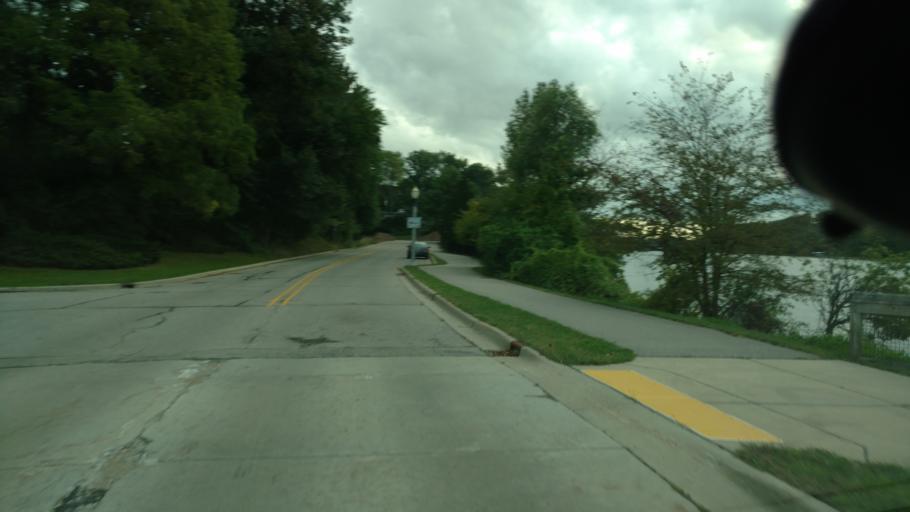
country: US
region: Michigan
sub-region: Ingham County
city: Edgemont Park
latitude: 42.7164
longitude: -84.5934
